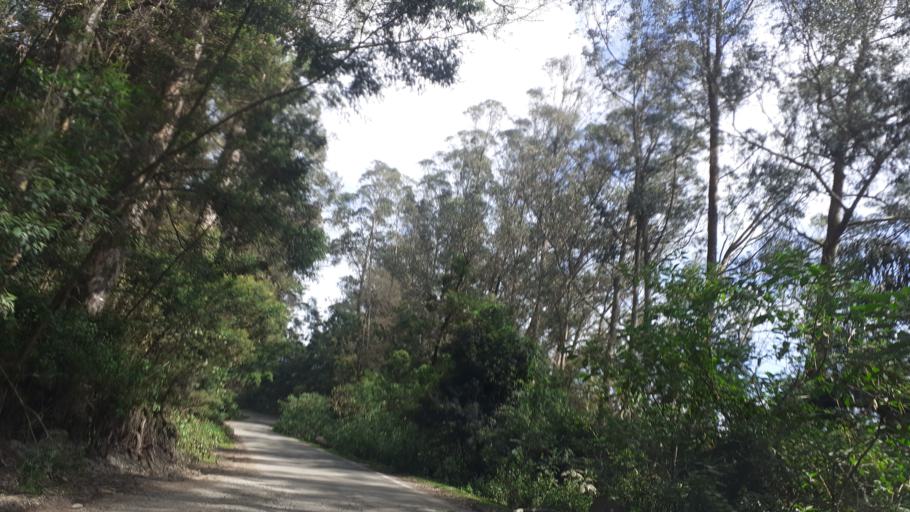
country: IN
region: Tamil Nadu
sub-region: Dindigul
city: Kodaikanal
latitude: 10.2315
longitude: 77.4241
